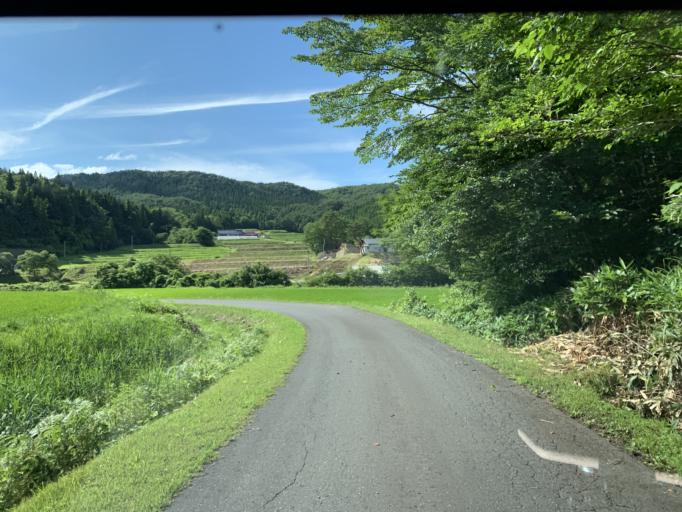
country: JP
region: Iwate
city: Ichinoseki
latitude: 38.9275
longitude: 140.9548
